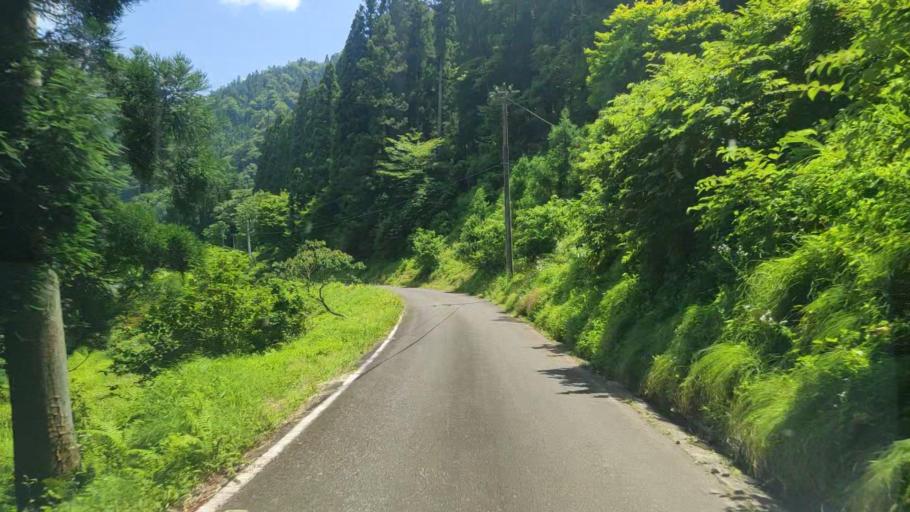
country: JP
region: Fukui
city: Ono
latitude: 35.7498
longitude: 136.5800
